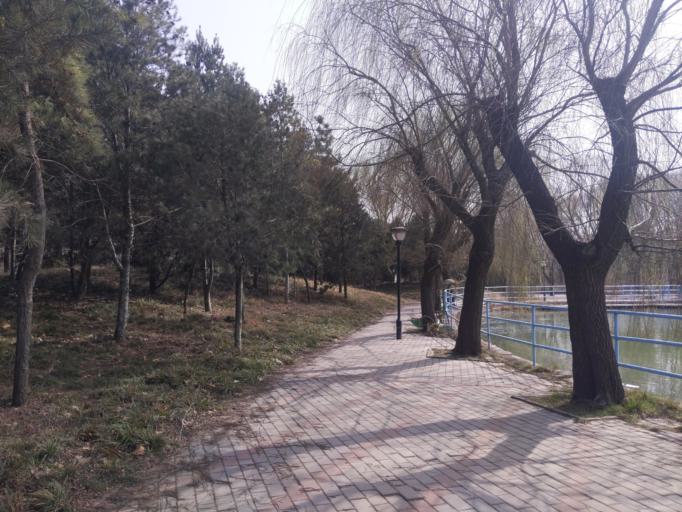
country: CN
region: Henan Sheng
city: Puyang
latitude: 35.7787
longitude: 114.9625
